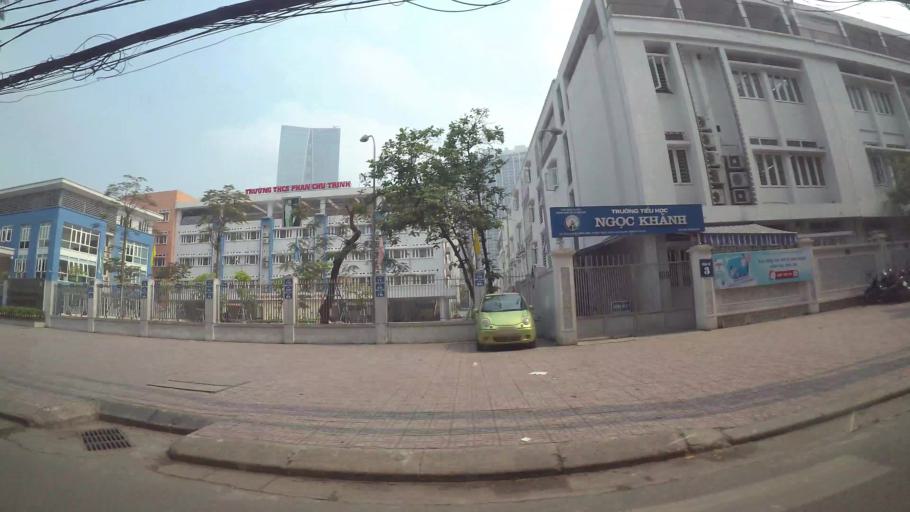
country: VN
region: Ha Noi
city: Cau Giay
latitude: 21.0273
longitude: 105.8146
